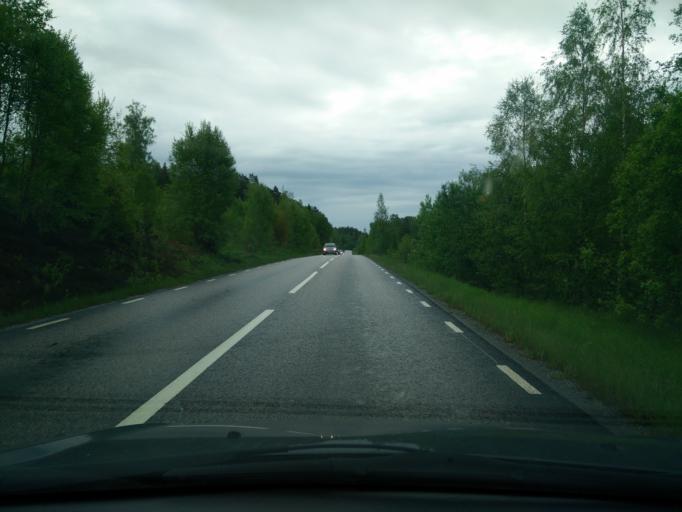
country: SE
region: Stockholm
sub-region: Norrtalje Kommun
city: Norrtalje
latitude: 59.7807
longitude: 18.8267
